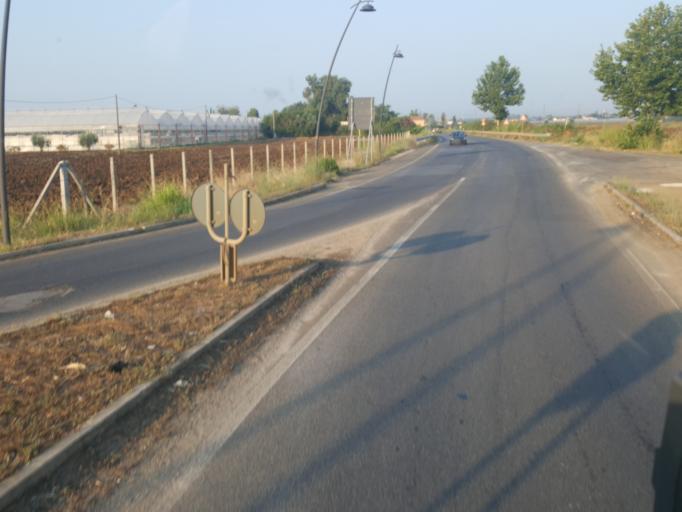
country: IT
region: Latium
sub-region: Provincia di Latina
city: Sezze Scalo
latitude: 41.4772
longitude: 13.0222
